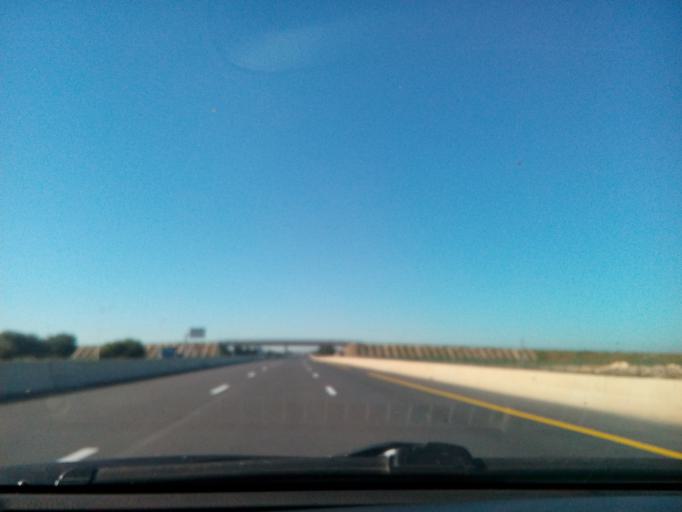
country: DZ
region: Relizane
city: Djidiouia
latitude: 35.9177
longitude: 0.7619
